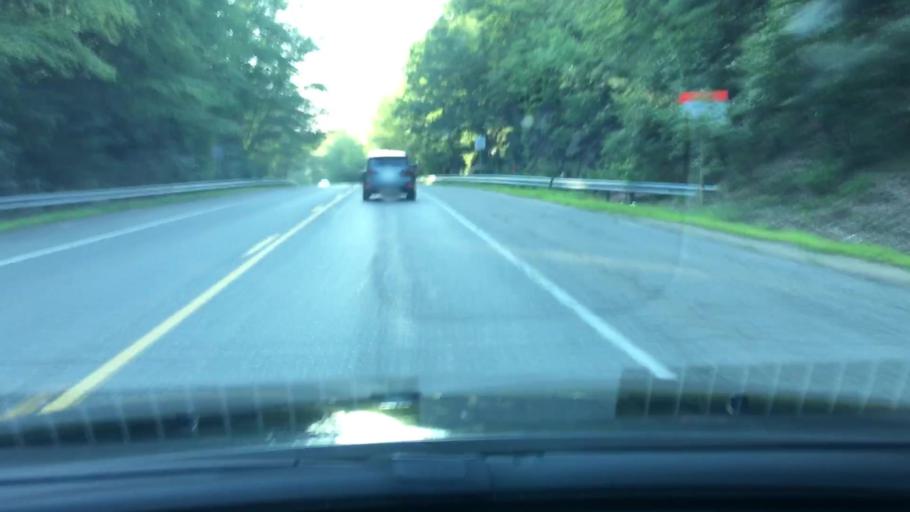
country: US
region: Massachusetts
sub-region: Worcester County
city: West Boylston
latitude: 42.3374
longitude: -71.7489
